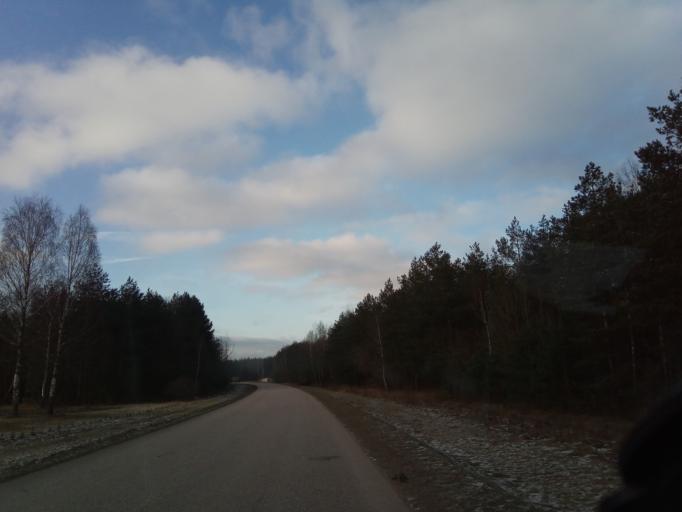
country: LT
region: Alytaus apskritis
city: Druskininkai
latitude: 53.9803
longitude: 24.2441
